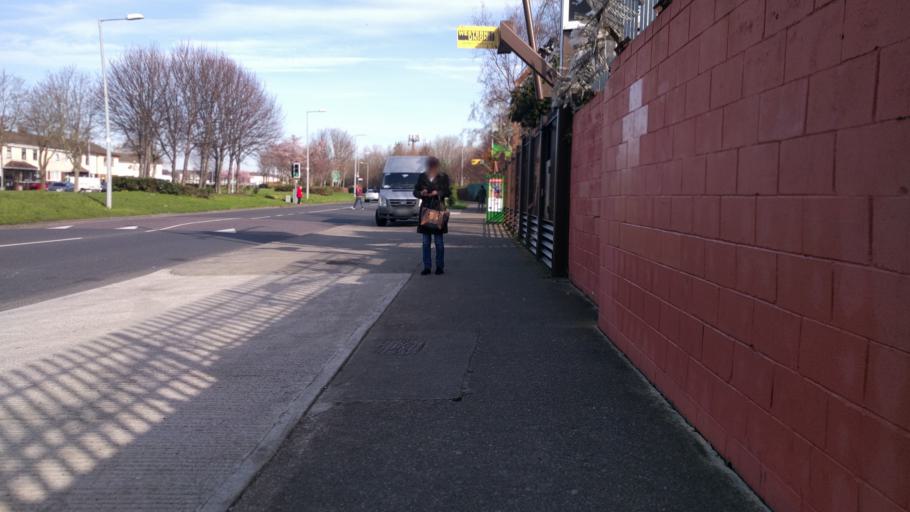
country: IE
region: Leinster
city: Tallaght
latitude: 53.2803
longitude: -6.3838
